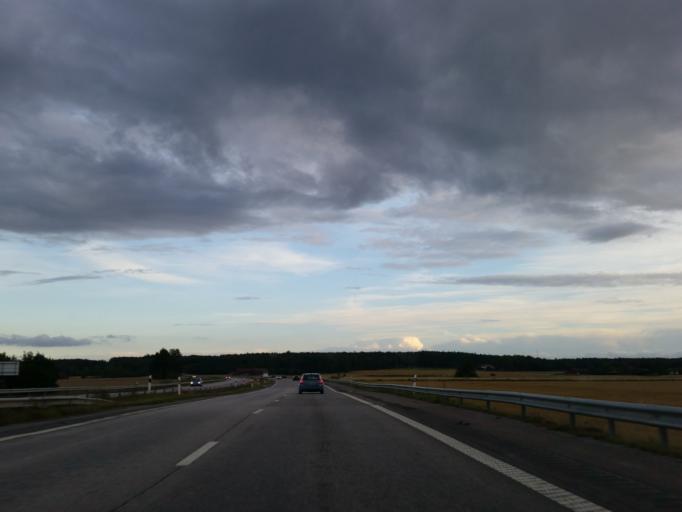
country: SE
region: Uppsala
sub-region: Uppsala Kommun
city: Saevja
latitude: 59.8149
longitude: 17.7548
